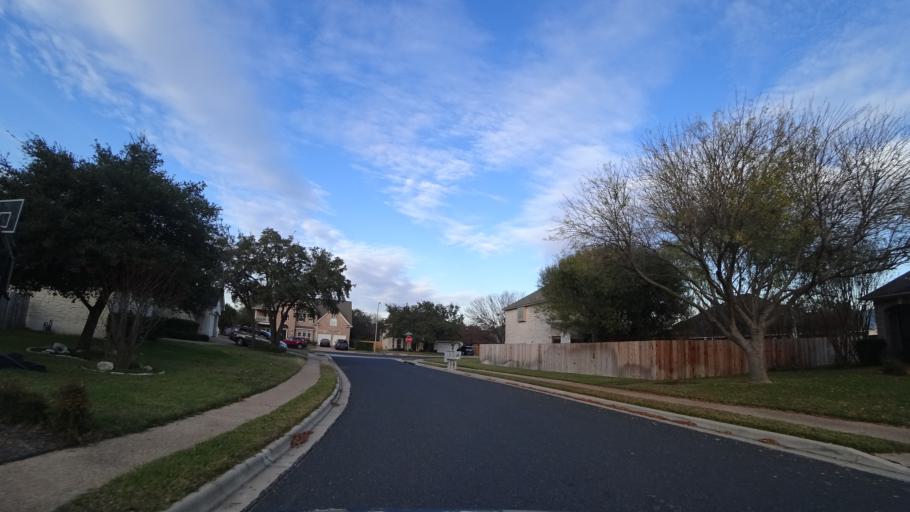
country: US
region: Texas
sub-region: Williamson County
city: Brushy Creek
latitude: 30.4960
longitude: -97.7409
